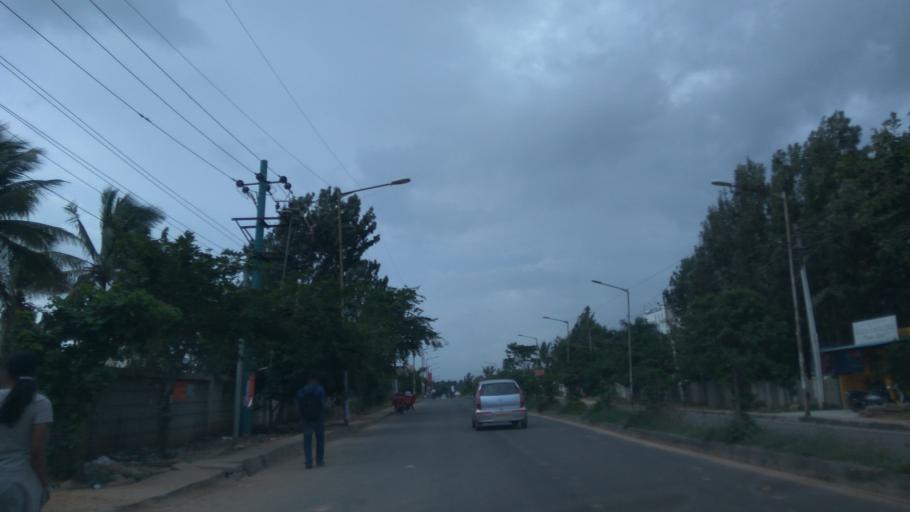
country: IN
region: Karnataka
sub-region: Bangalore Urban
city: Yelahanka
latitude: 13.0852
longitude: 77.6348
